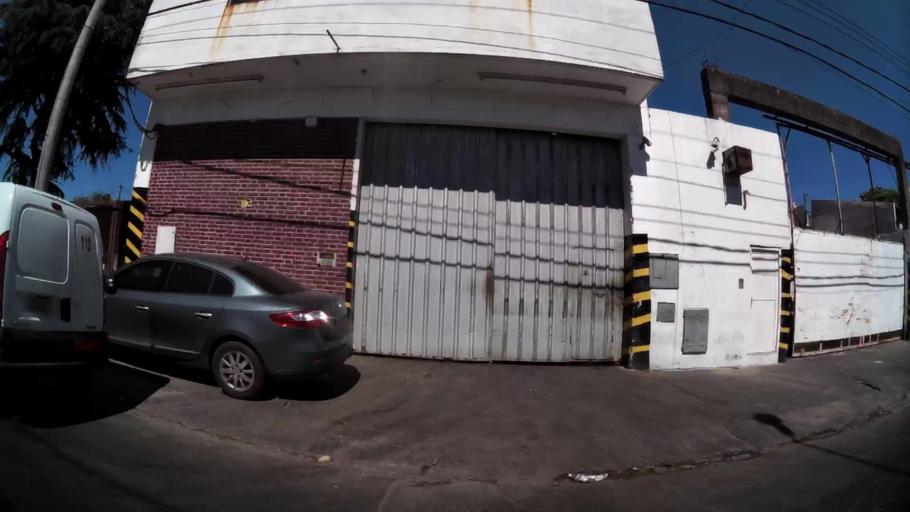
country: AR
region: Buenos Aires
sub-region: Partido de Tigre
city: Tigre
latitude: -34.4934
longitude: -58.6121
